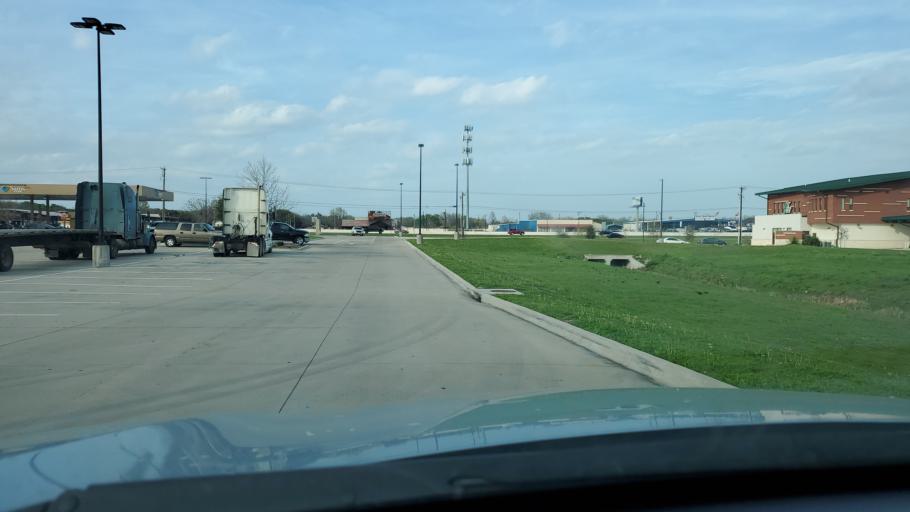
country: US
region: Texas
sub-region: Bell County
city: Harker Heights
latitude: 31.0711
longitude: -97.6785
